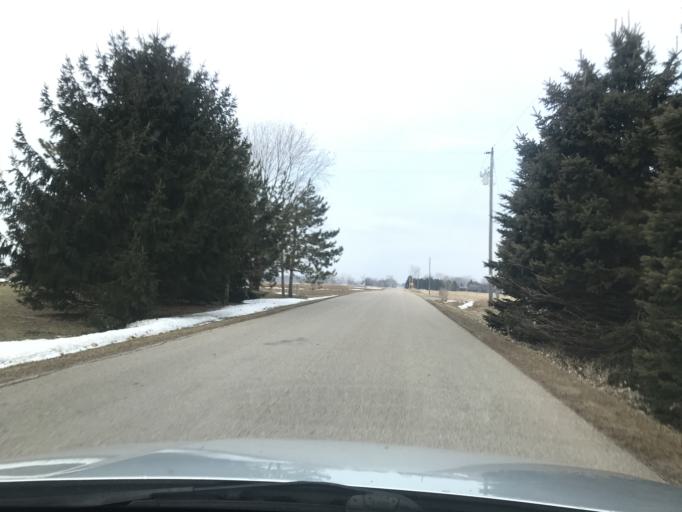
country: US
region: Wisconsin
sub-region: Oconto County
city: Oconto Falls
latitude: 44.8507
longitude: -88.1617
